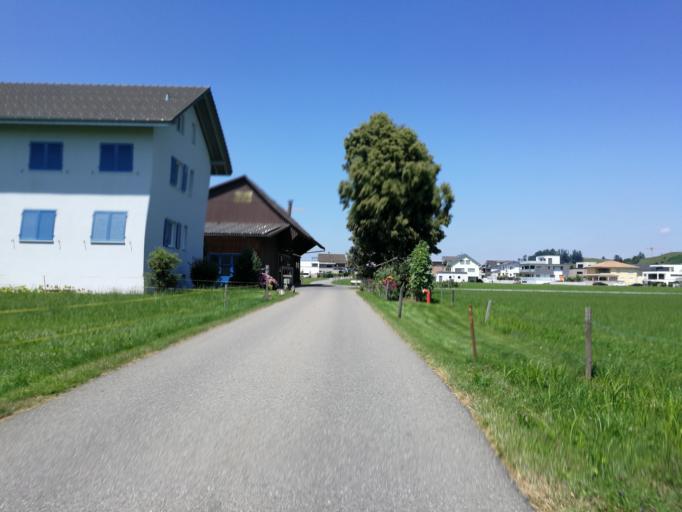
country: CH
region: Schwyz
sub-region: Bezirk March
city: Schubelbach
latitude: 47.1866
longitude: 8.9052
